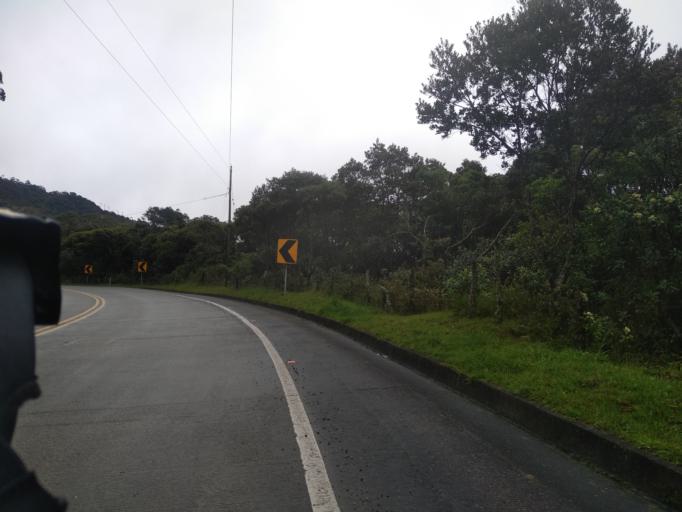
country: EC
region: Loja
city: Catamayo
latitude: -3.8639
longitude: -79.2814
